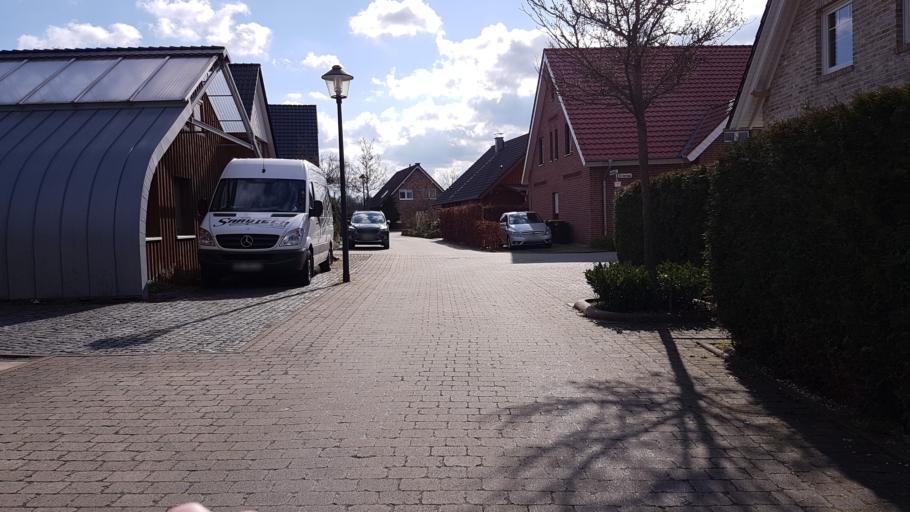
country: DE
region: North Rhine-Westphalia
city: Olfen
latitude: 51.6997
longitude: 7.3782
